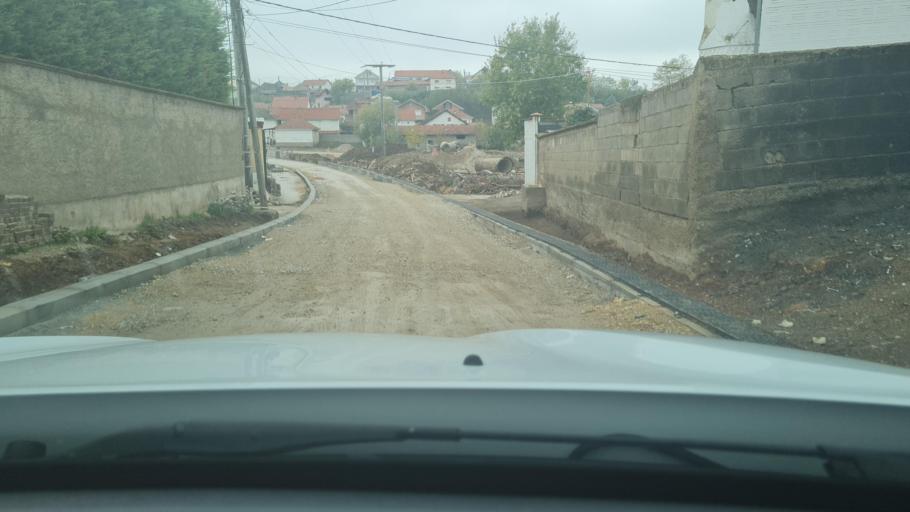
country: MK
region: Opstina Lipkovo
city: Matejche
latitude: 42.1103
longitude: 21.6183
